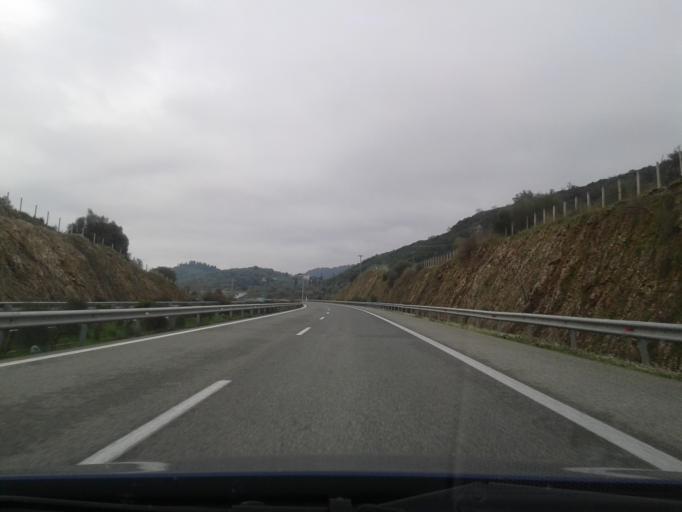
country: GR
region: West Greece
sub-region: Nomos Aitolias kai Akarnanias
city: Angelokastro
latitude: 38.5956
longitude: 21.2338
